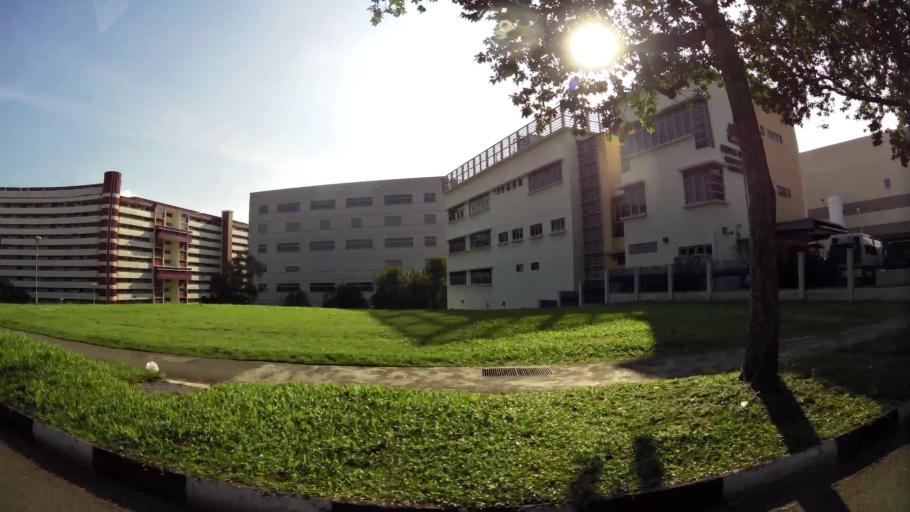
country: SG
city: Singapore
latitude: 1.3238
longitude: 103.9195
